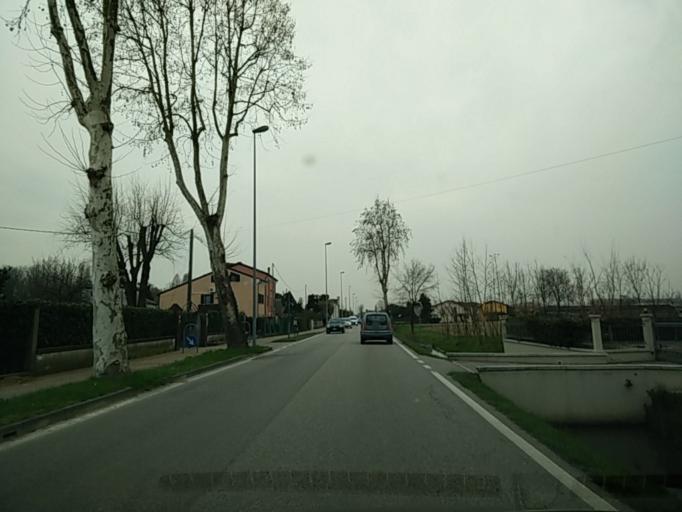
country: IT
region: Veneto
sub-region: Provincia di Venezia
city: Noale
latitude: 45.5538
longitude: 12.0392
